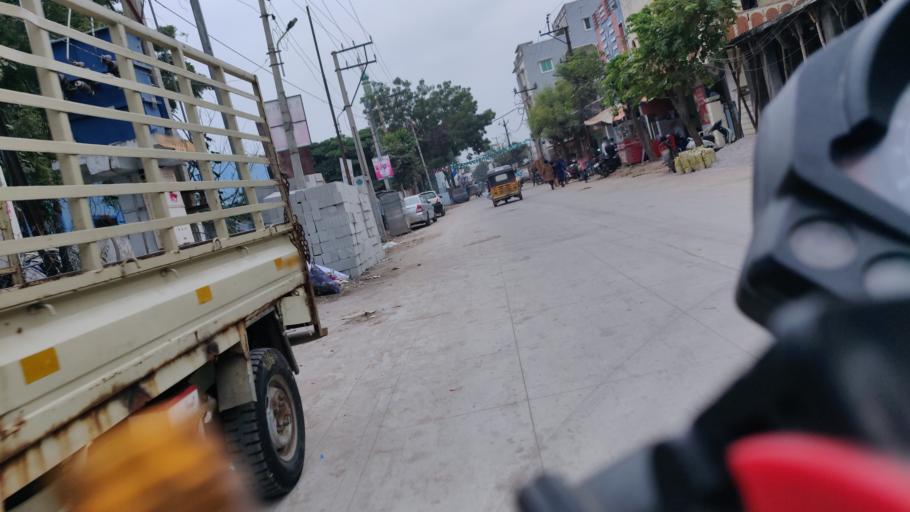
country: IN
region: Telangana
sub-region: Rangareddi
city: Kukatpalli
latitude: 17.4528
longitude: 78.4082
